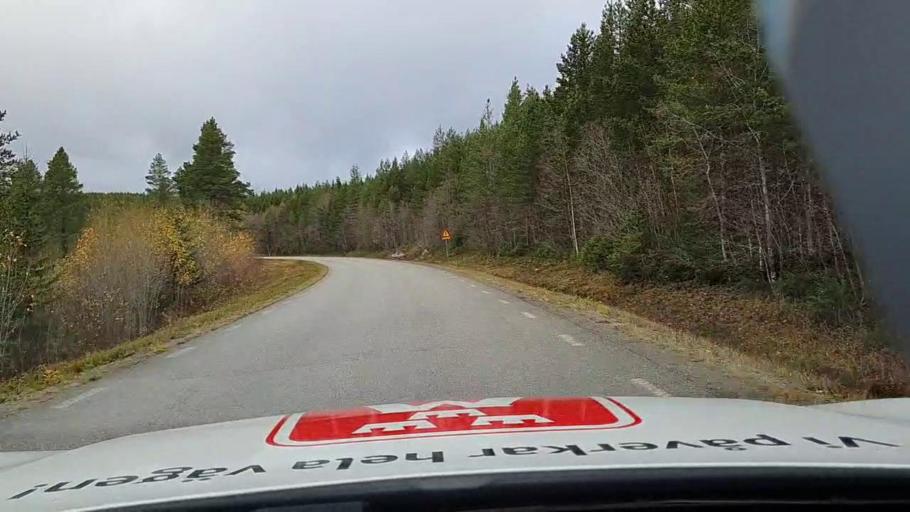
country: SE
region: Jaemtland
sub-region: Bergs Kommun
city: Hoverberg
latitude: 63.0367
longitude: 14.0396
